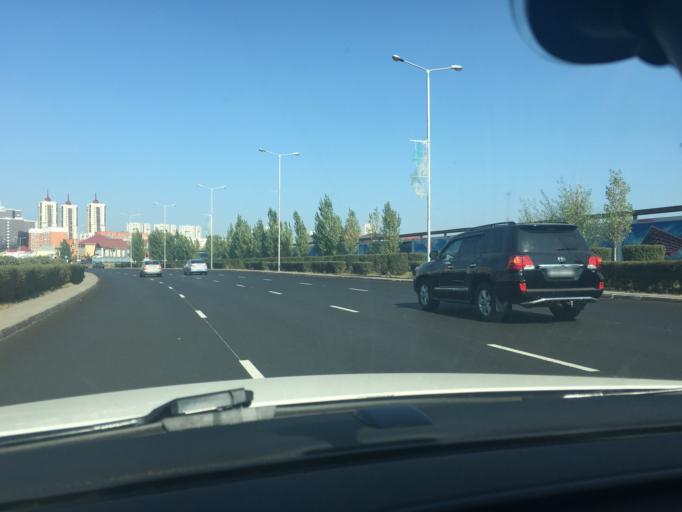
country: KZ
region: Astana Qalasy
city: Astana
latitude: 51.1301
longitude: 71.4713
